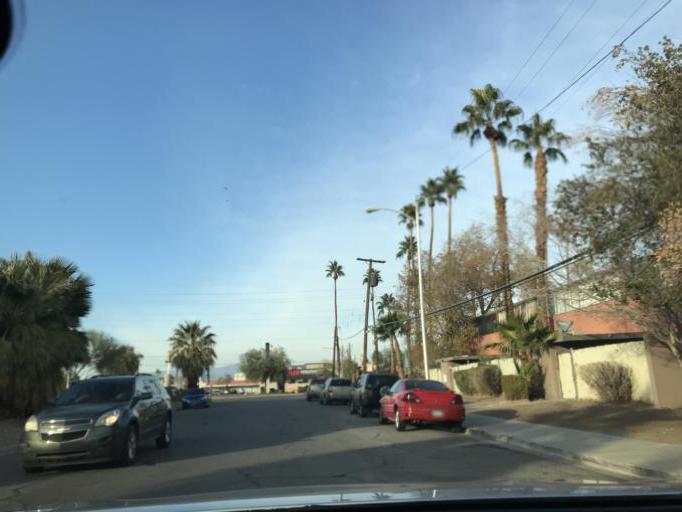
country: US
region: Nevada
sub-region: Clark County
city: Winchester
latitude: 36.1431
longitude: -115.1457
